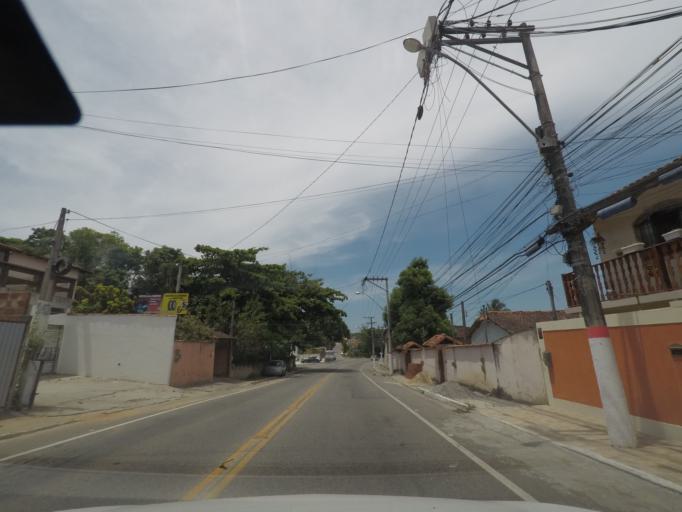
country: BR
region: Rio de Janeiro
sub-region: Marica
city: Marica
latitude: -22.9283
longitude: -42.8208
